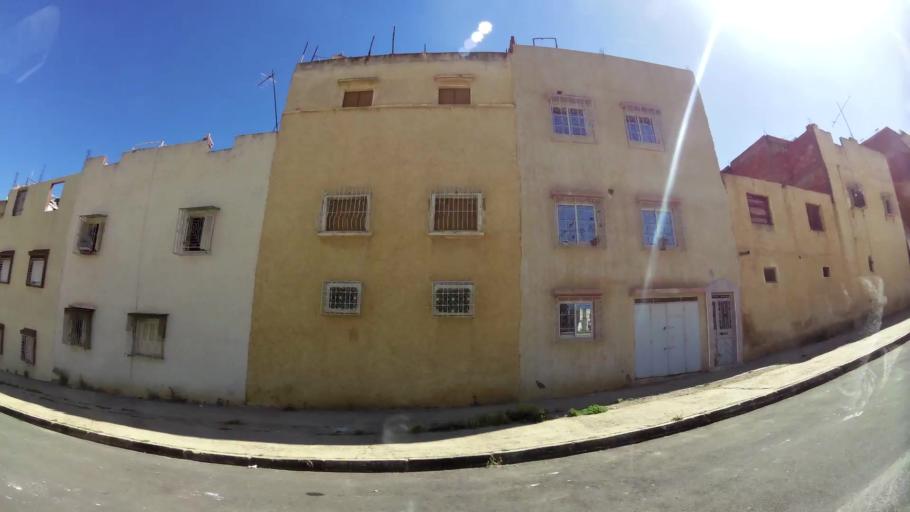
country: MA
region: Meknes-Tafilalet
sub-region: Meknes
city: Meknes
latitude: 33.9074
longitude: -5.5398
